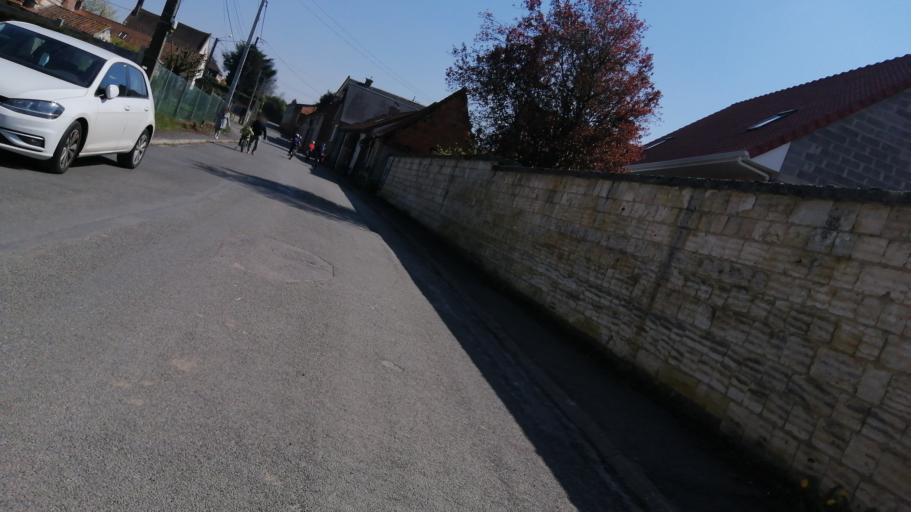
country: FR
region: Nord-Pas-de-Calais
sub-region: Departement du Pas-de-Calais
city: Duisans
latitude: 50.3079
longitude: 2.6561
